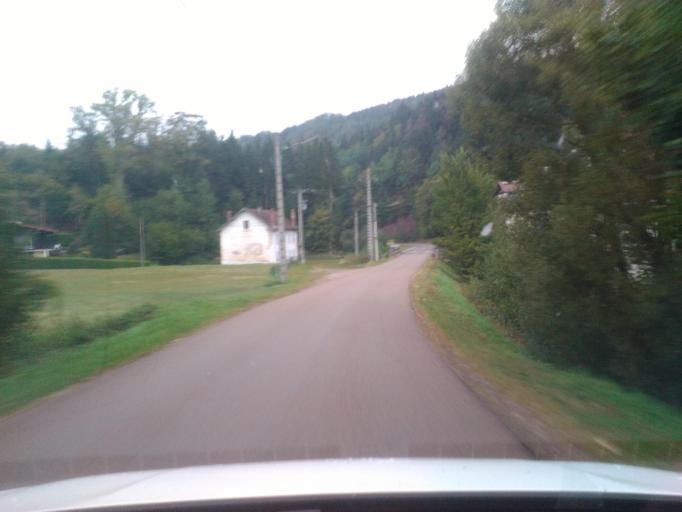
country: FR
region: Lorraine
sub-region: Departement des Vosges
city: Senones
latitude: 48.3373
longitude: 6.9854
